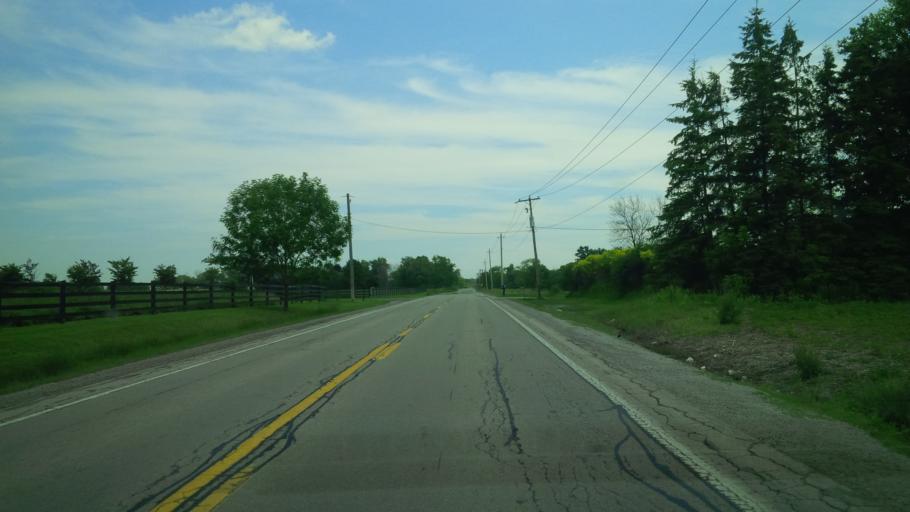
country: CA
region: Ontario
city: Burlington
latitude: 43.4403
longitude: -79.8650
